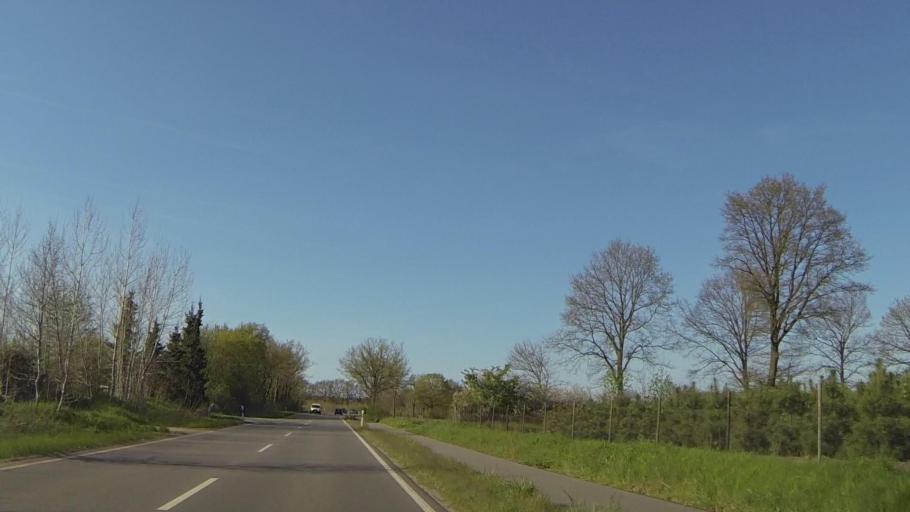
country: DE
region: Schleswig-Holstein
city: Wedel
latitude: 53.6066
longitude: 9.7152
